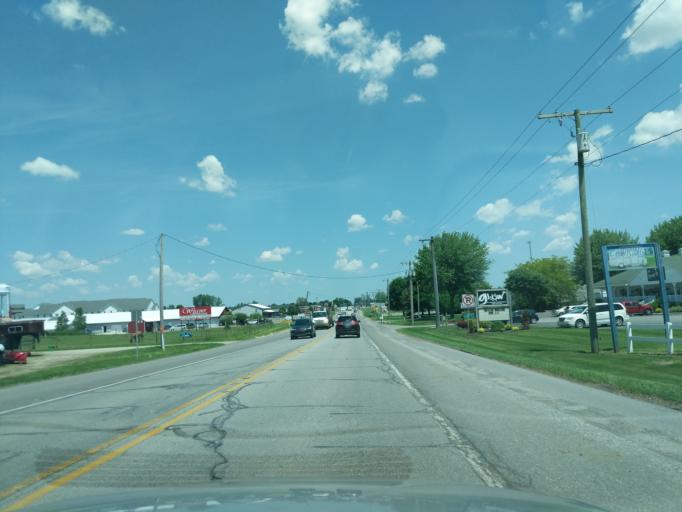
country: US
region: Indiana
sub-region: Elkhart County
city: Middlebury
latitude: 41.6626
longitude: -85.5803
